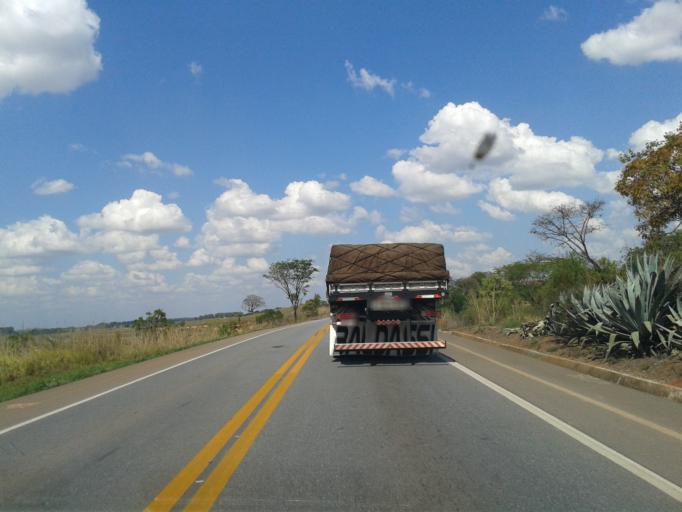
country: BR
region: Minas Gerais
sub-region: Luz
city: Luz
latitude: -19.7434
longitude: -45.8384
